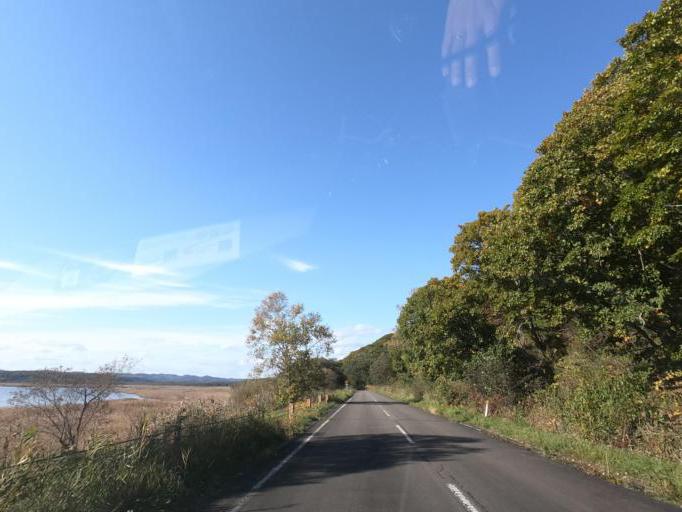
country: JP
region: Hokkaido
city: Obihiro
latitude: 42.6165
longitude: 143.5437
